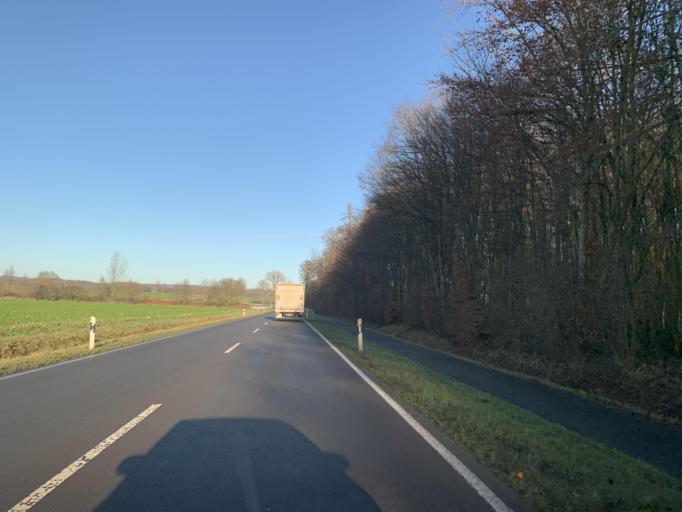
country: DE
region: North Rhine-Westphalia
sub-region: Regierungsbezirk Munster
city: Dulmen
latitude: 51.8723
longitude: 7.2871
